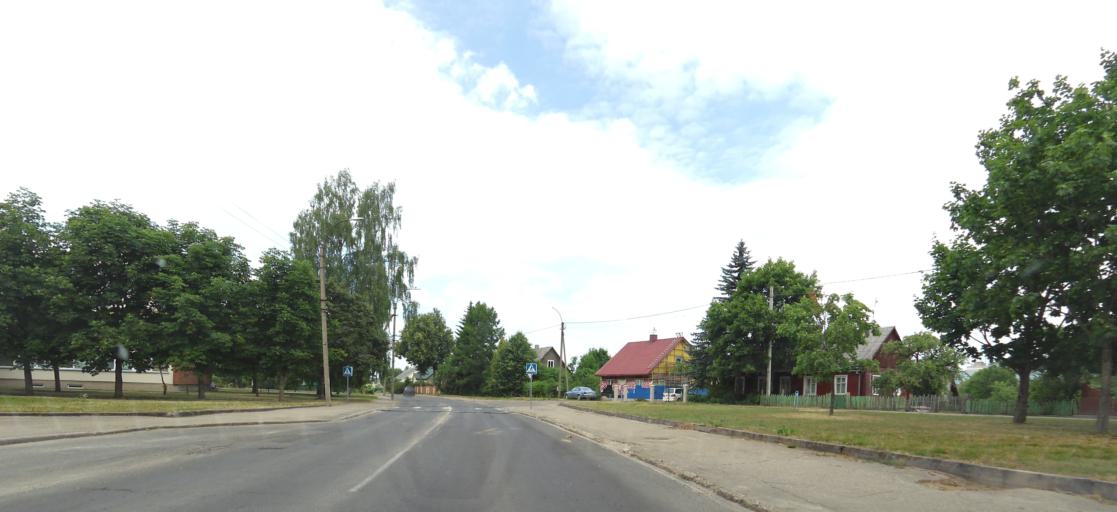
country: LT
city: Sirvintos
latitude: 55.0477
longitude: 24.9487
